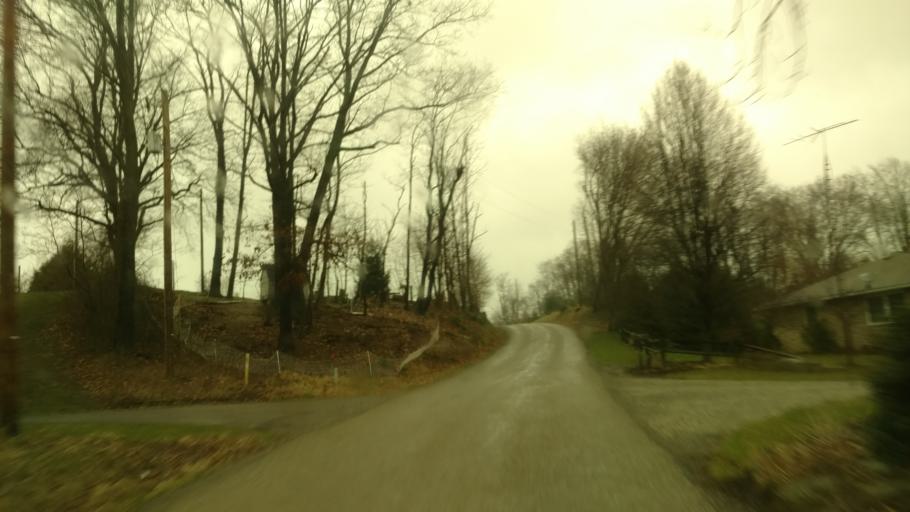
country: US
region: Ohio
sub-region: Holmes County
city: Millersburg
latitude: 40.5309
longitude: -81.8407
